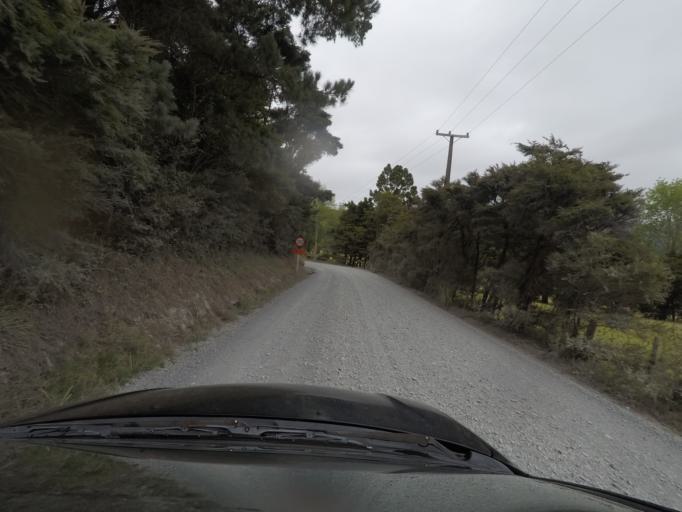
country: NZ
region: Auckland
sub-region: Auckland
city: Warkworth
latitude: -36.2600
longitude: 174.7244
